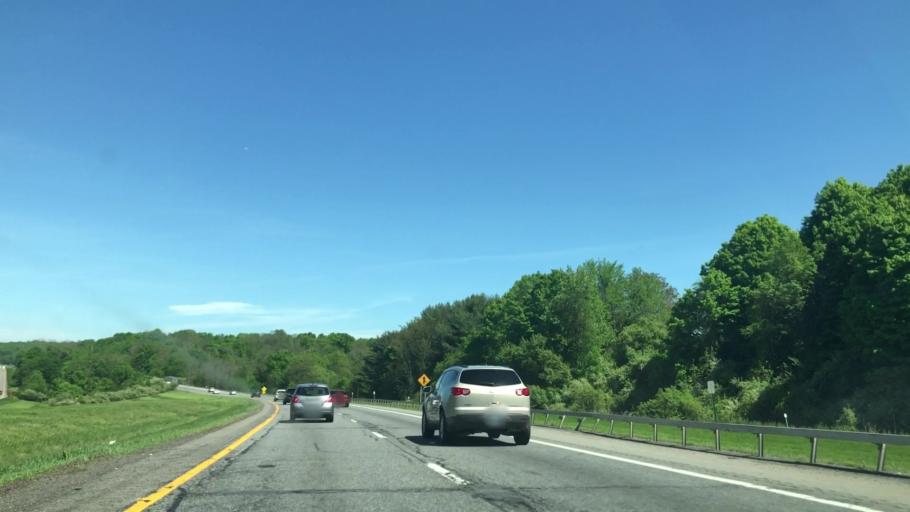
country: US
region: New York
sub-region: Putnam County
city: Peach Lake
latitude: 41.3829
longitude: -73.5816
